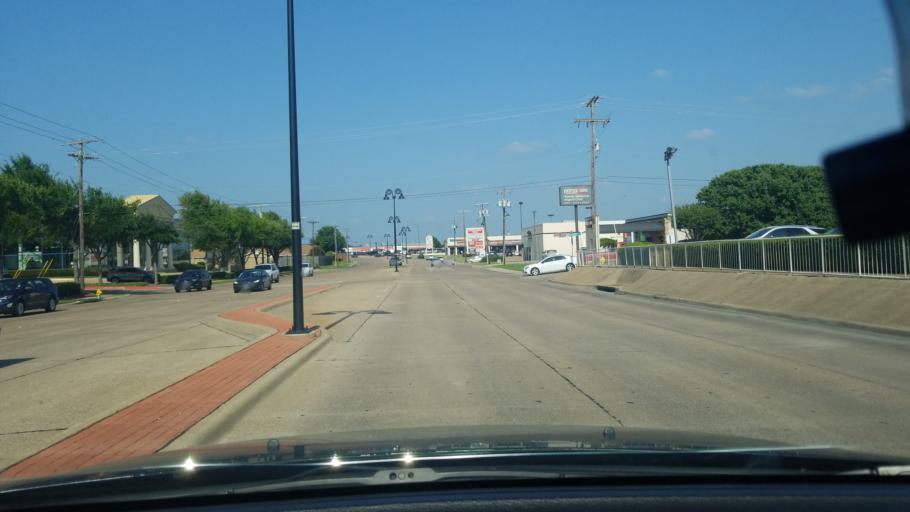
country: US
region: Texas
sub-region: Dallas County
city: Mesquite
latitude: 32.8107
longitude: -96.6152
